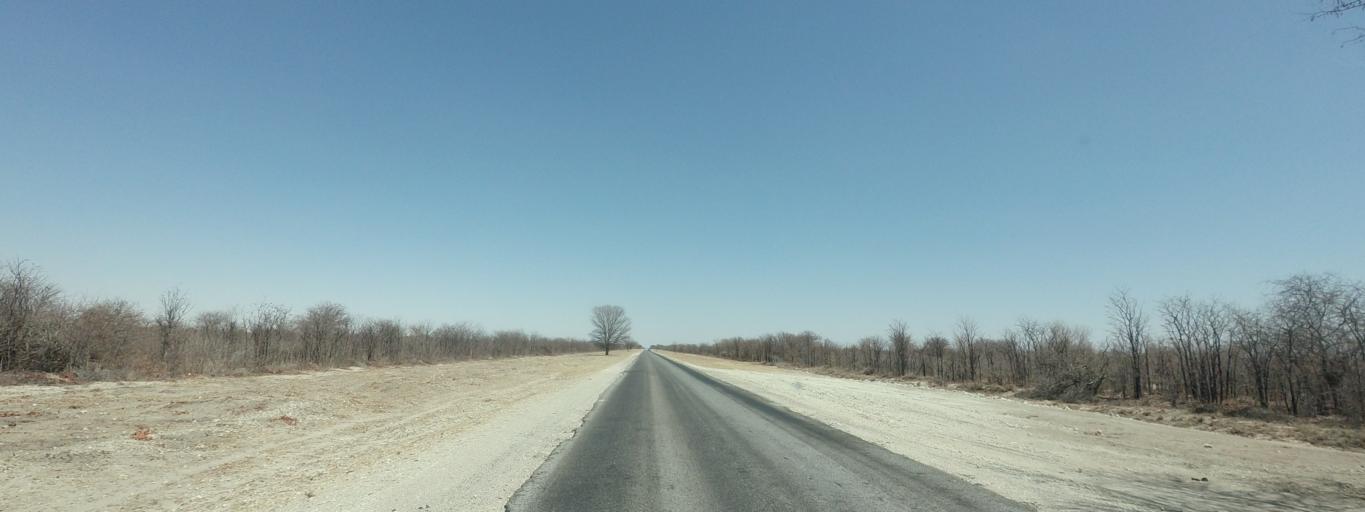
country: BW
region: North East
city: Dukwe
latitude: -20.3955
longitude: 26.3548
